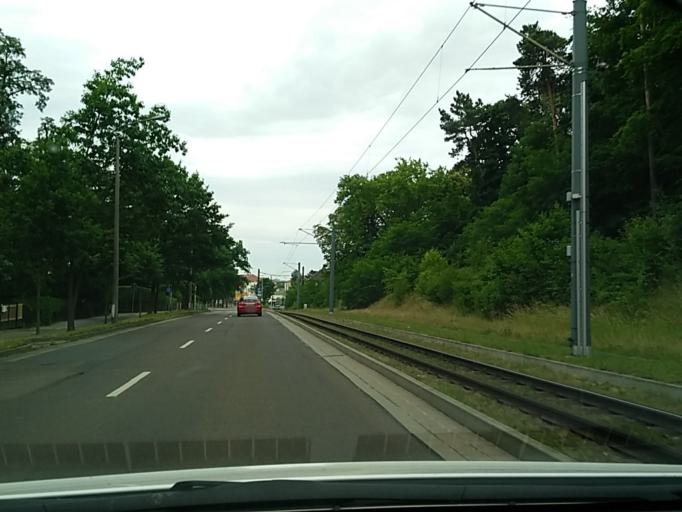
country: DE
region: Saxony-Anhalt
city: Halle Neustadt
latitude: 51.5029
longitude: 11.9300
